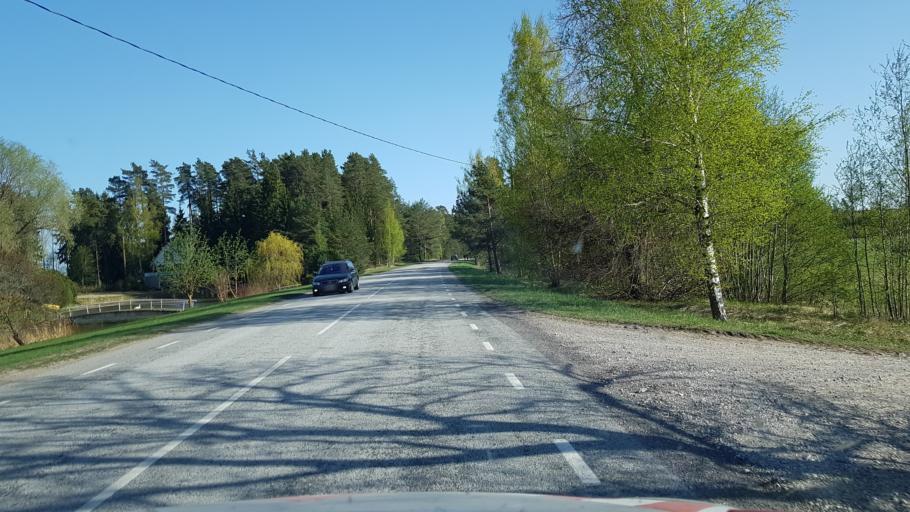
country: EE
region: Paernumaa
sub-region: Paikuse vald
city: Paikuse
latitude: 58.3553
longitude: 24.6634
